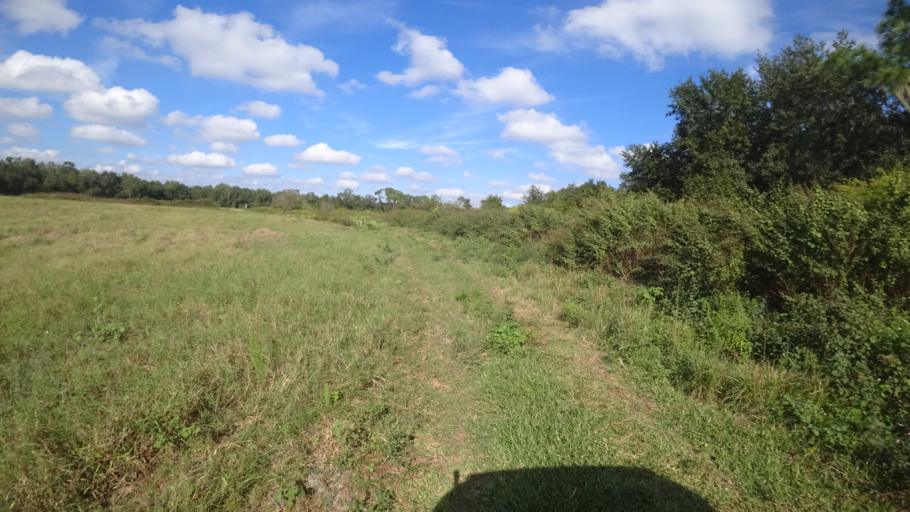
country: US
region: Florida
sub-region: Sarasota County
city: Lake Sarasota
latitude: 27.3732
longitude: -82.1566
